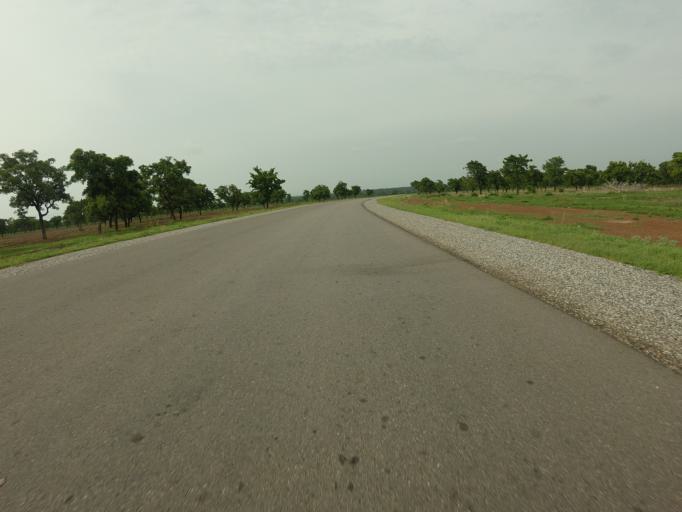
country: GH
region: Northern
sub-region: Yendi
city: Yendi
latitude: 9.8066
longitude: -0.1135
